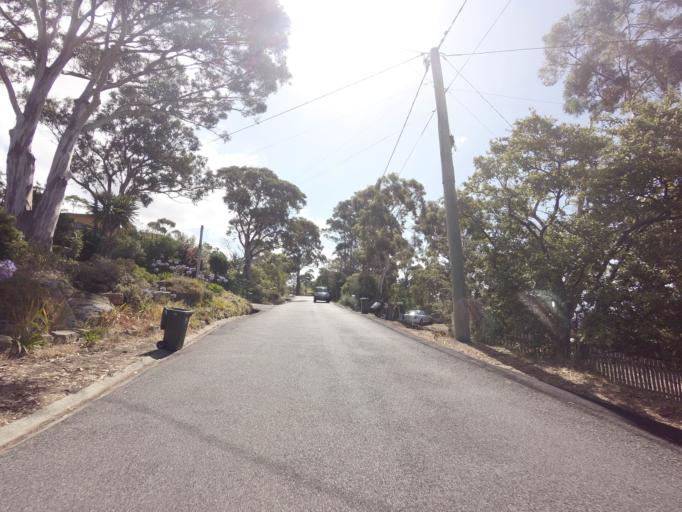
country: AU
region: Tasmania
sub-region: Hobart
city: Dynnyrne
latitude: -42.9120
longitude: 147.3251
